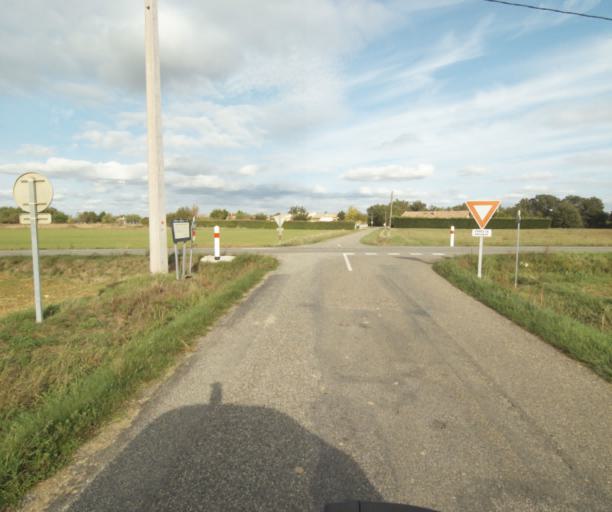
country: FR
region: Midi-Pyrenees
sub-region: Departement du Tarn-et-Garonne
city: Verdun-sur-Garonne
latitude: 43.8360
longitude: 1.1580
